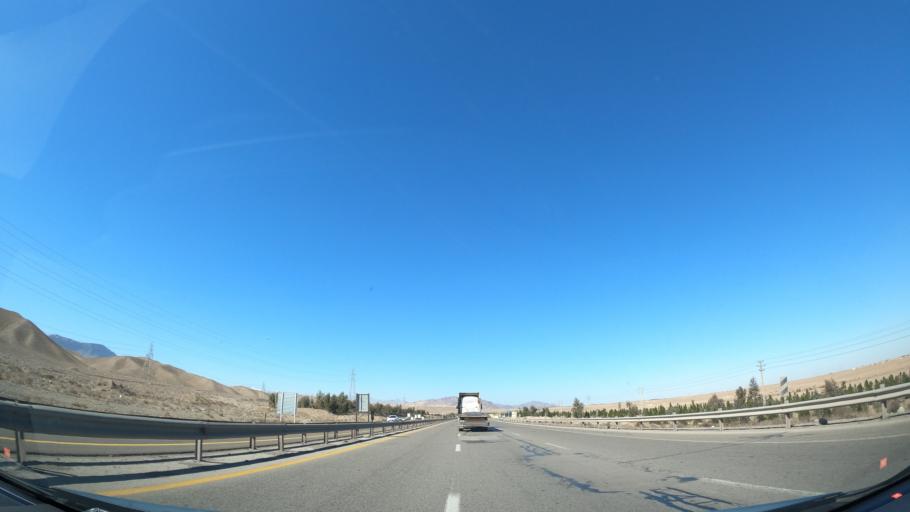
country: IR
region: Isfahan
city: Kashan
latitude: 33.9653
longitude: 51.3473
